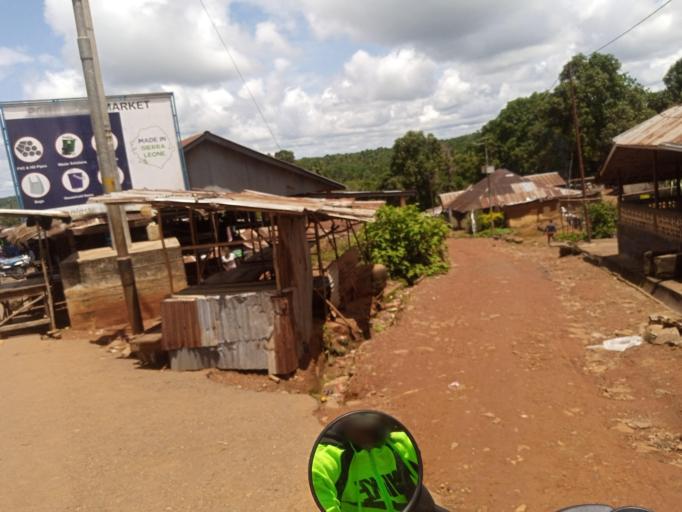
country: SL
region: Northern Province
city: Port Loko
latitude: 8.7644
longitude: -12.7903
